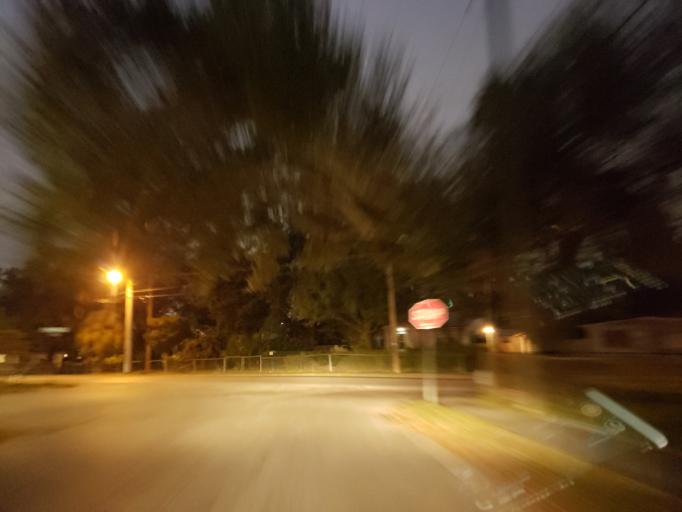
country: US
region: Florida
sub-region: Hillsborough County
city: University
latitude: 28.0251
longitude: -82.4382
